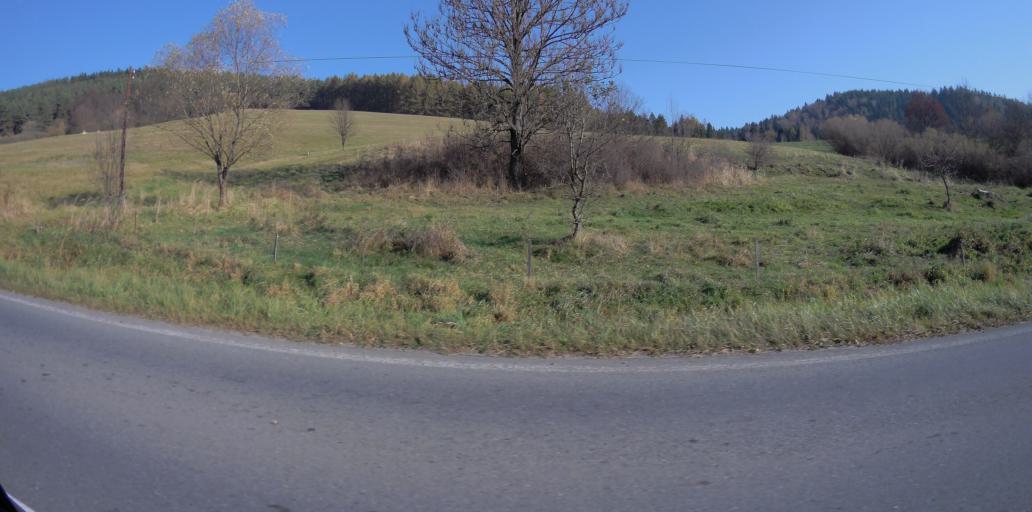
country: PL
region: Subcarpathian Voivodeship
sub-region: Powiat bieszczadzki
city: Ustrzyki Dolne
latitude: 49.4865
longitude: 22.6603
